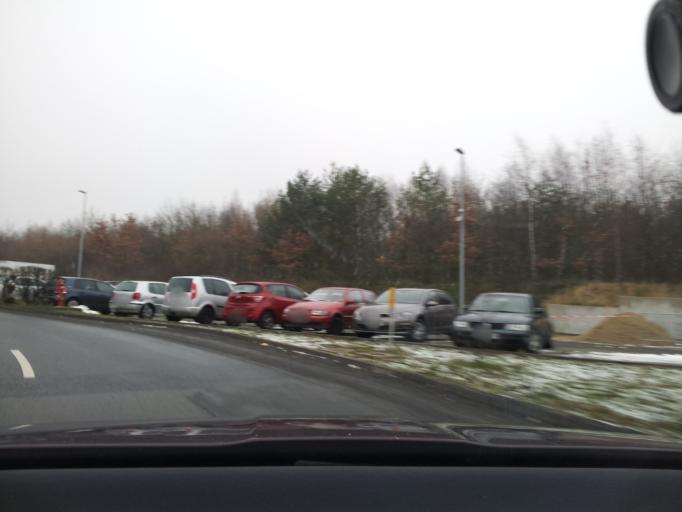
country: DE
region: Brandenburg
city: Wildau
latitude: 52.3148
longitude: 13.6128
